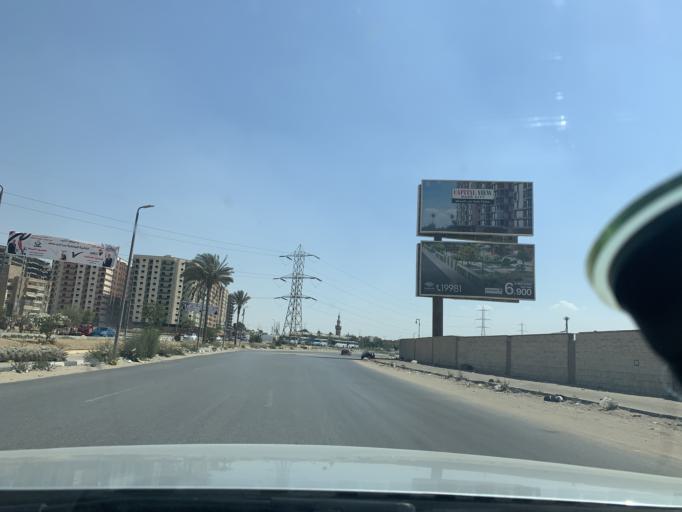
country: EG
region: Muhafazat al Qahirah
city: Cairo
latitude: 30.0375
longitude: 31.3552
